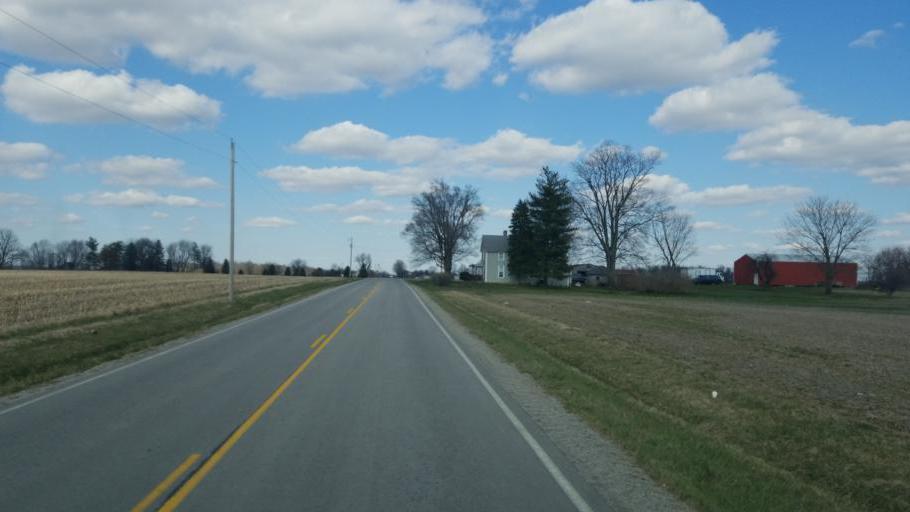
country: US
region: Ohio
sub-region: Highland County
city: Greenfield
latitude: 39.3142
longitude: -83.4289
